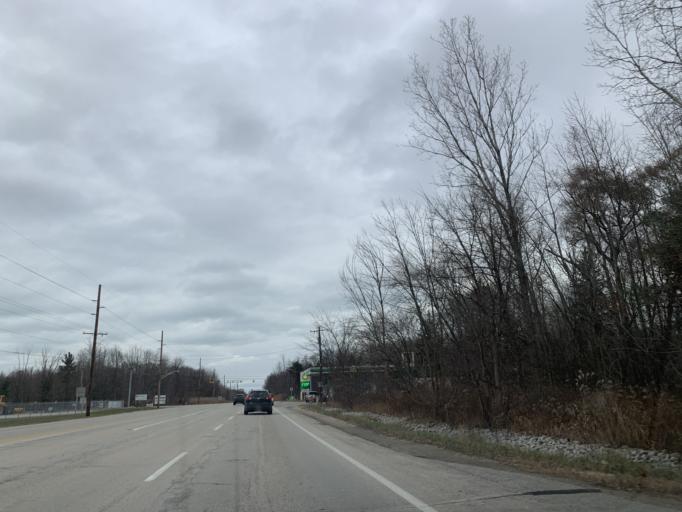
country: US
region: Indiana
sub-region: LaPorte County
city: Long Beach
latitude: 41.7223
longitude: -86.8260
